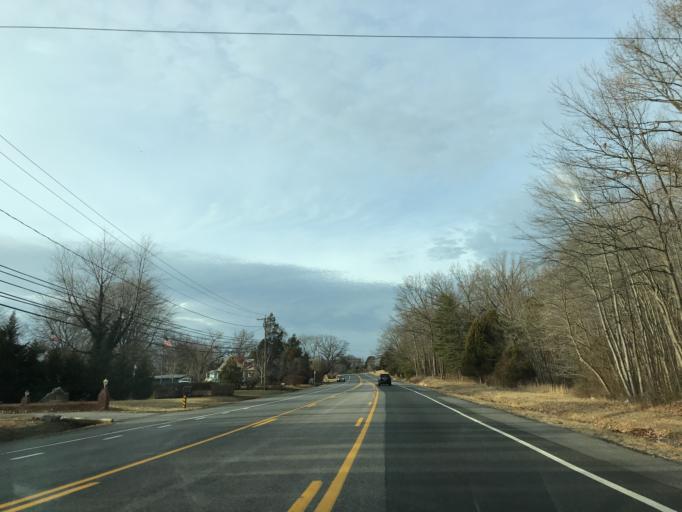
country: US
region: Maryland
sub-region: Harford County
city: Joppatowne
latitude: 39.4515
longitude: -76.3550
